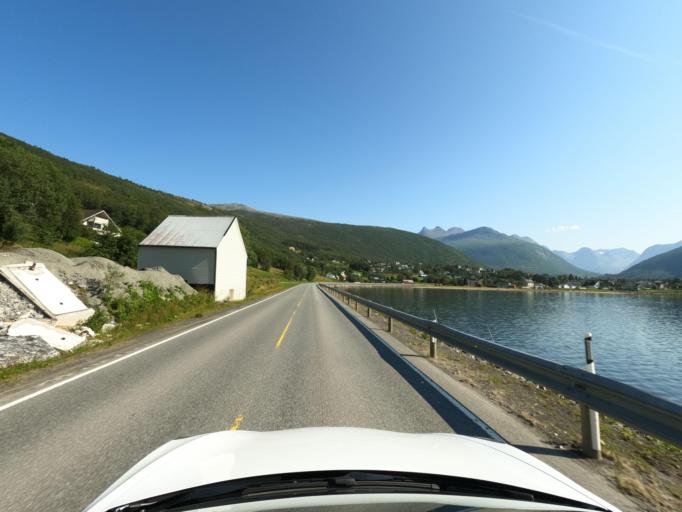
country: NO
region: Nordland
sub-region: Narvik
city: Bjerkvik
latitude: 68.3813
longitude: 17.5921
